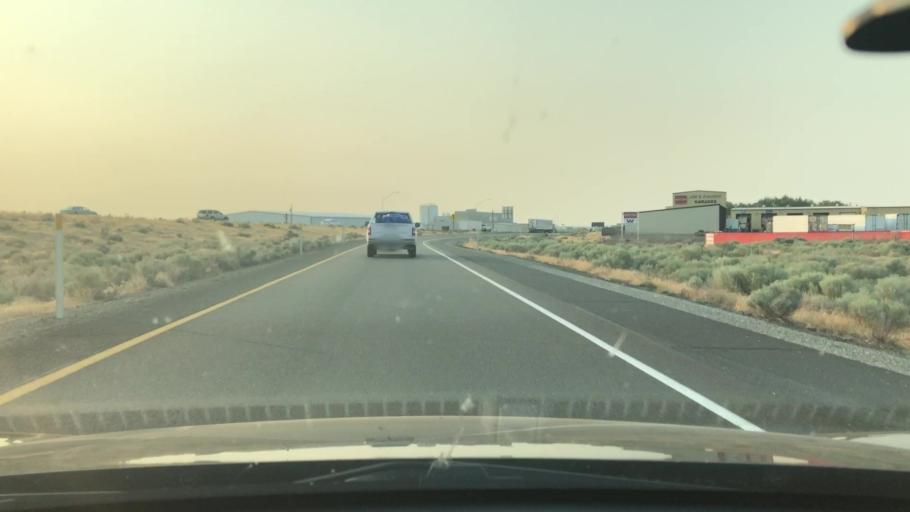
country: US
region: Washington
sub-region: Franklin County
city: Pasco
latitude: 46.2540
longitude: -119.0821
